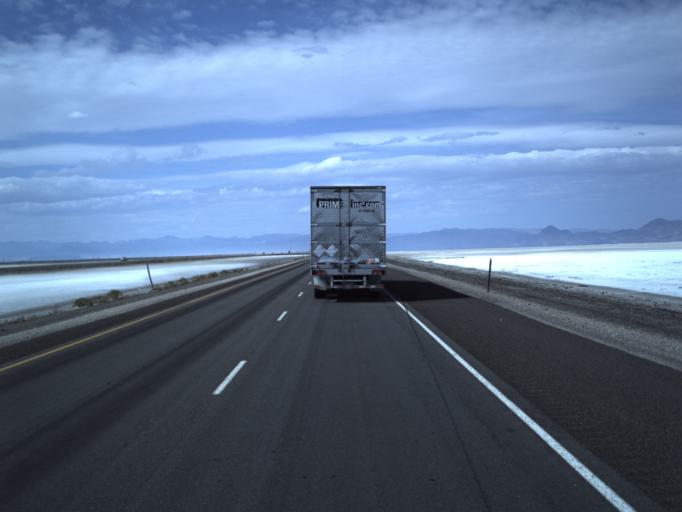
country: US
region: Utah
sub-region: Tooele County
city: Wendover
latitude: 40.7358
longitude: -113.6780
